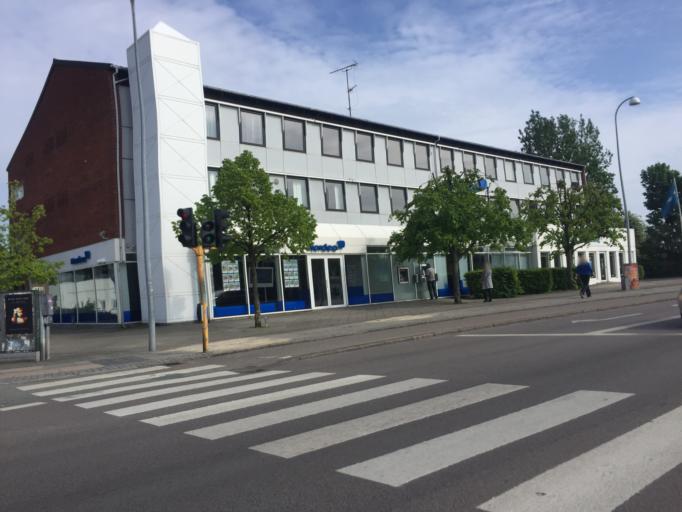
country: DK
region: Capital Region
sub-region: Hvidovre Kommune
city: Hvidovre
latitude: 55.6634
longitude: 12.4738
